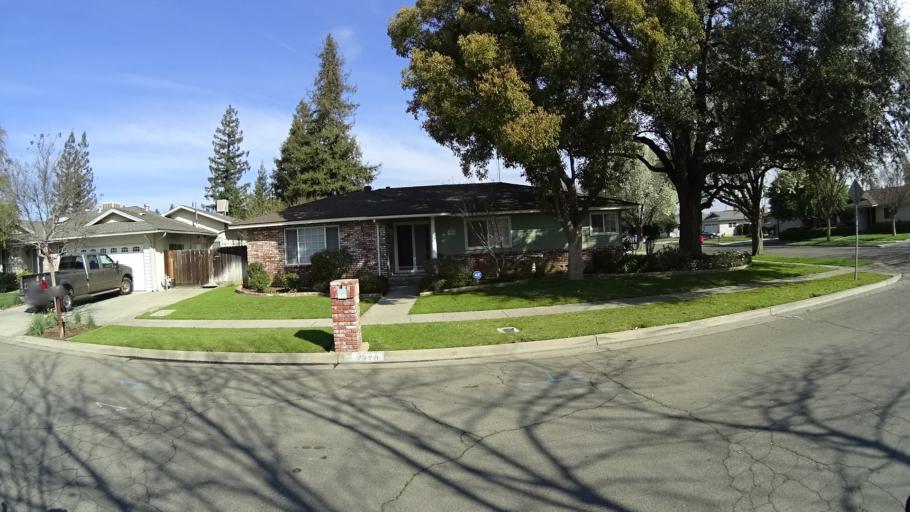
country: US
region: California
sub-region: Fresno County
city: Clovis
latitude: 36.8351
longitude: -119.7483
